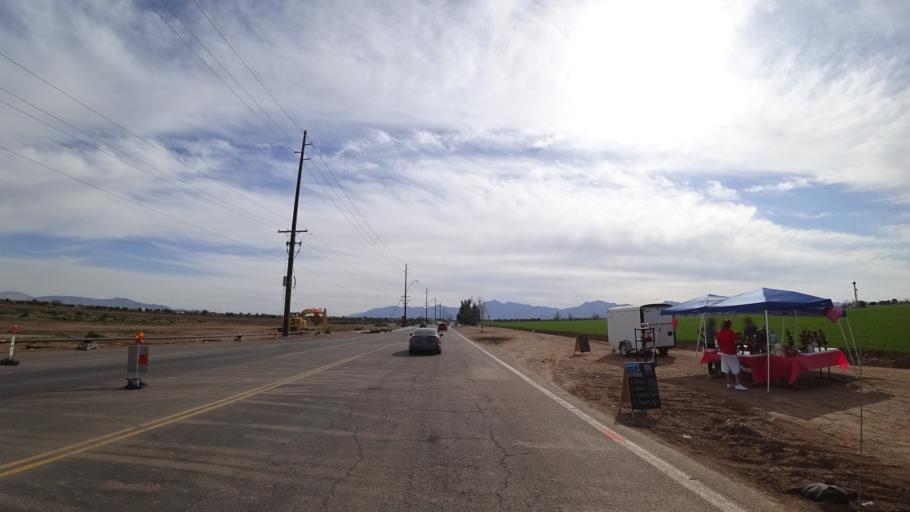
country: US
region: Arizona
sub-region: Maricopa County
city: Tolleson
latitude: 33.4351
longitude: -112.2552
